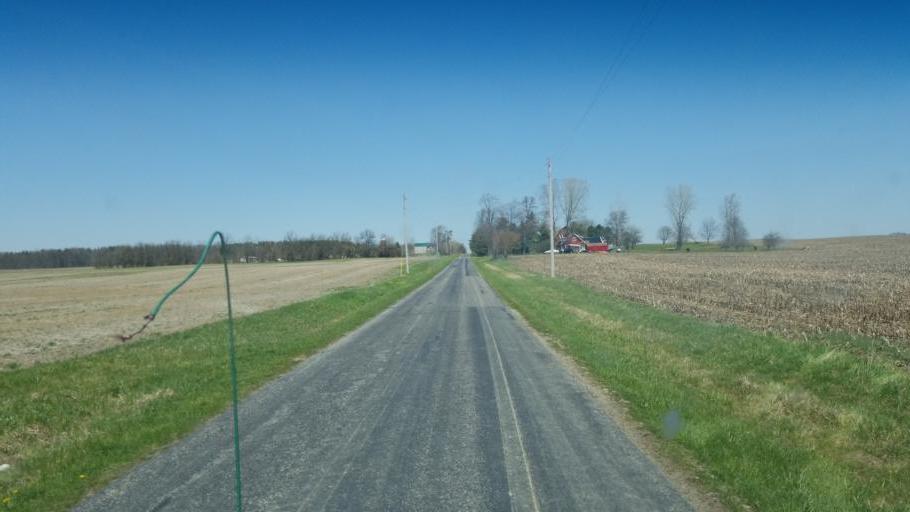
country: US
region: Ohio
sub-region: Huron County
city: New London
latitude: 41.0709
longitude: -82.4372
